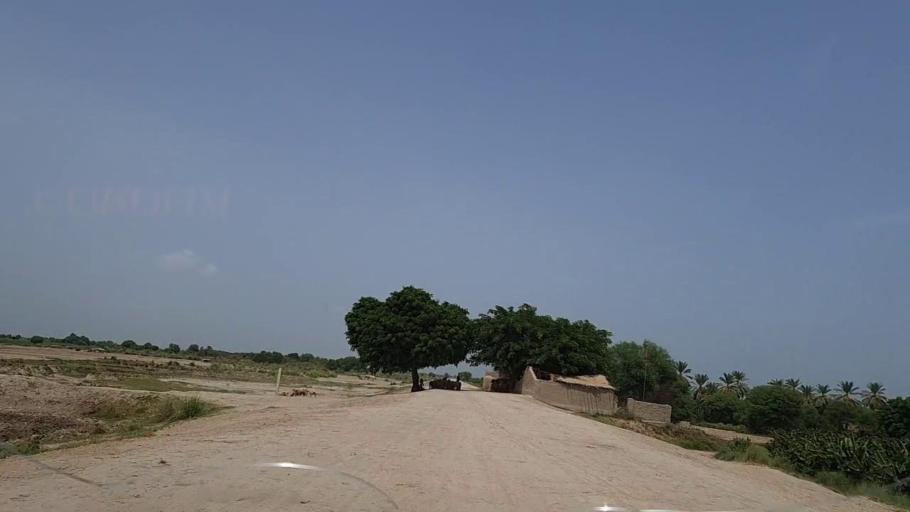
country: PK
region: Sindh
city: Kandiaro
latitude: 27.0476
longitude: 68.1177
